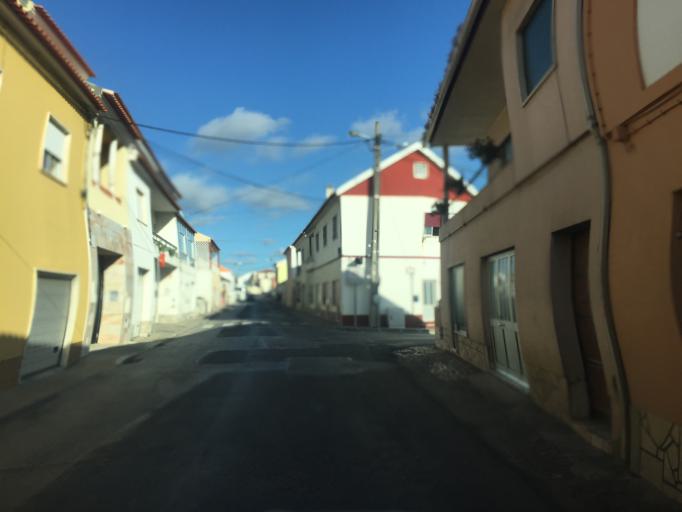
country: PT
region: Lisbon
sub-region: Torres Vedras
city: A dos Cunhados
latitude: 39.1499
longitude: -9.2966
